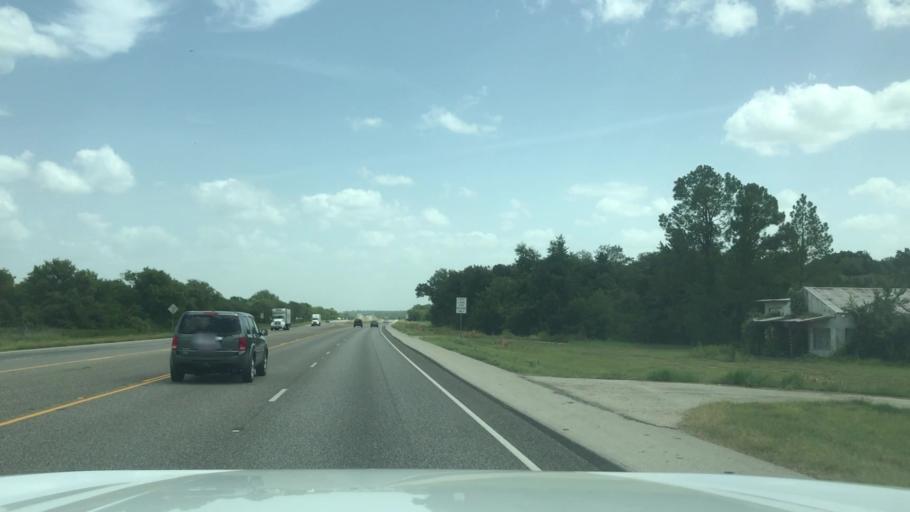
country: US
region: Texas
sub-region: Robertson County
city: Calvert
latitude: 30.9621
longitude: -96.6602
